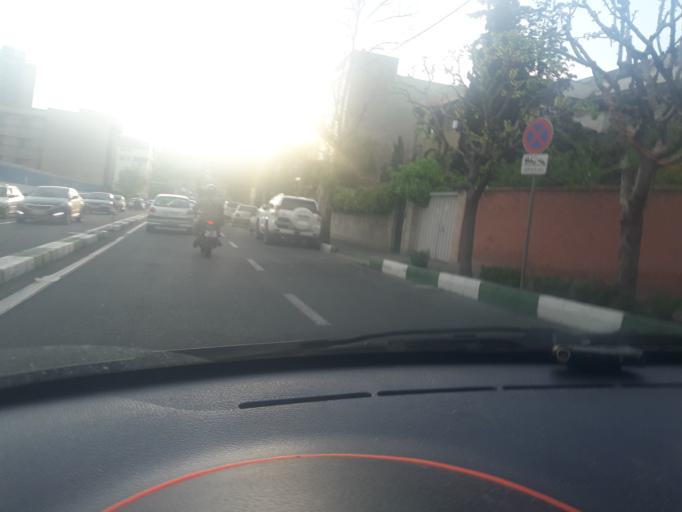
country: IR
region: Tehran
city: Tehran
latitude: 35.7466
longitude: 51.4048
